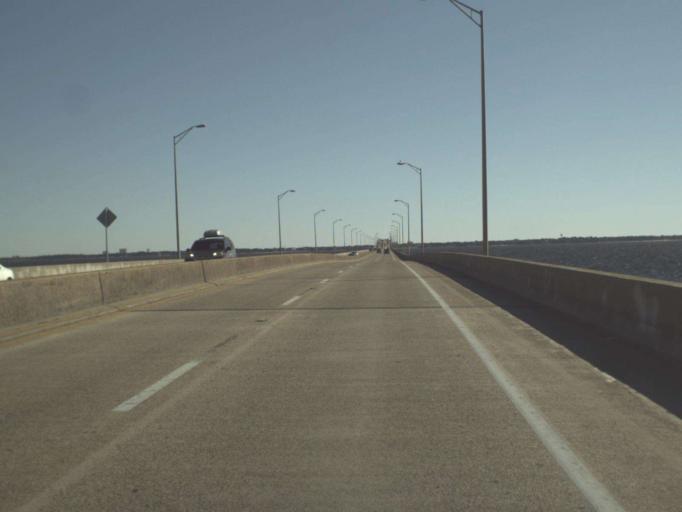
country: US
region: Florida
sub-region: Escambia County
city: East Pensacola Heights
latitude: 30.4072
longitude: -87.1898
